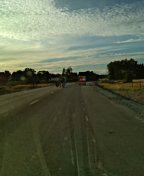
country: SE
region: Uppsala
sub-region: Enkopings Kommun
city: Irsta
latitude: 59.7216
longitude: 16.9625
